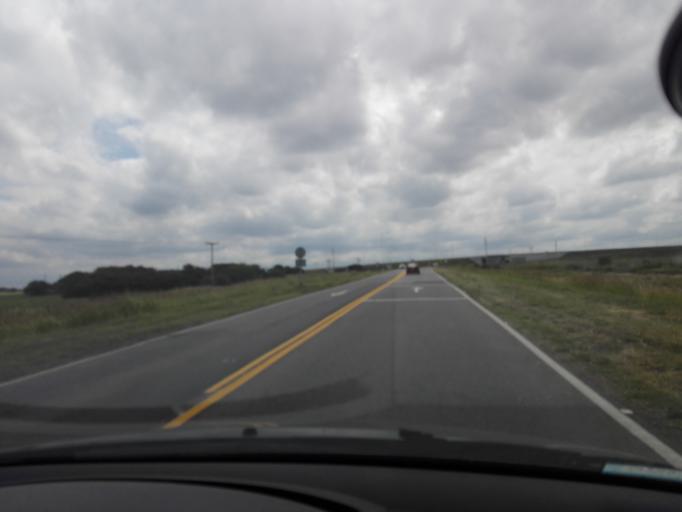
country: AR
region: Cordoba
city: Alta Gracia
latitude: -31.6521
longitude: -64.3101
